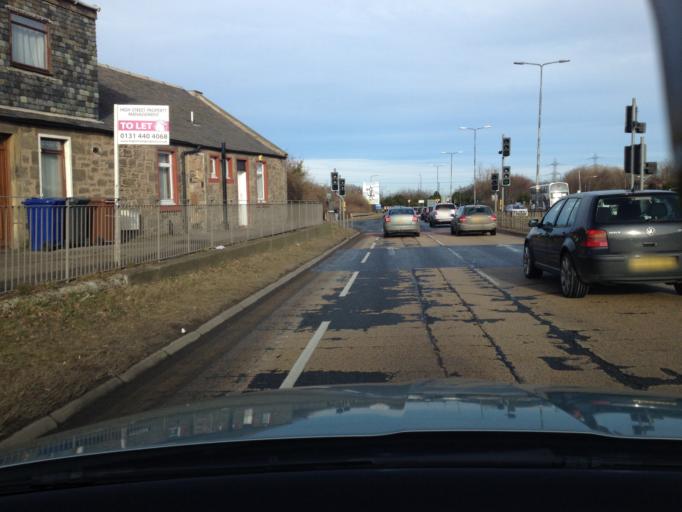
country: GB
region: Scotland
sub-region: Midlothian
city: Loanhead
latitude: 55.8868
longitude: -3.1646
